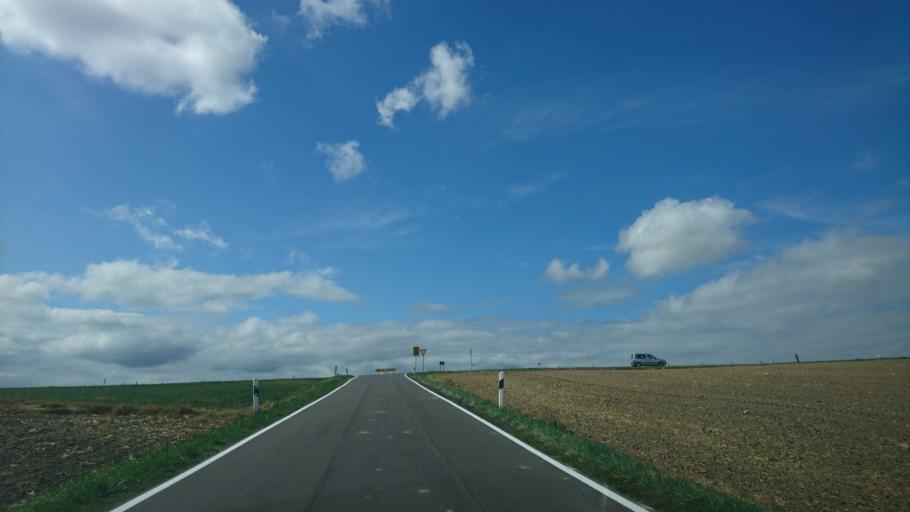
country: DE
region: Rheinland-Pfalz
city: Merzkirchen
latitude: 49.5816
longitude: 6.4814
